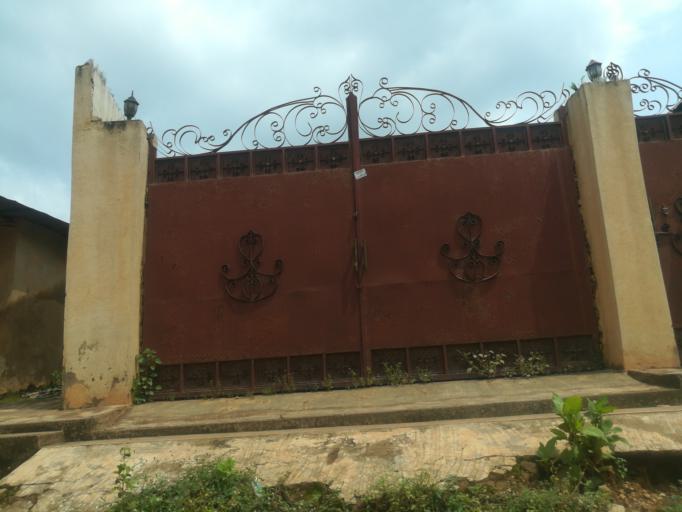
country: NG
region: Oyo
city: Moniya
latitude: 7.4521
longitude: 3.9568
